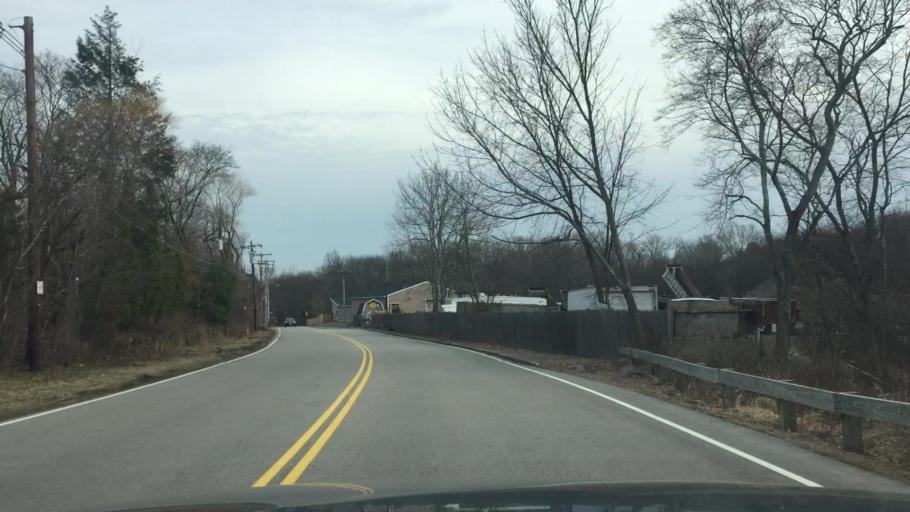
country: US
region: Massachusetts
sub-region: Norfolk County
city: Medway
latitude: 42.1374
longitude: -71.4498
